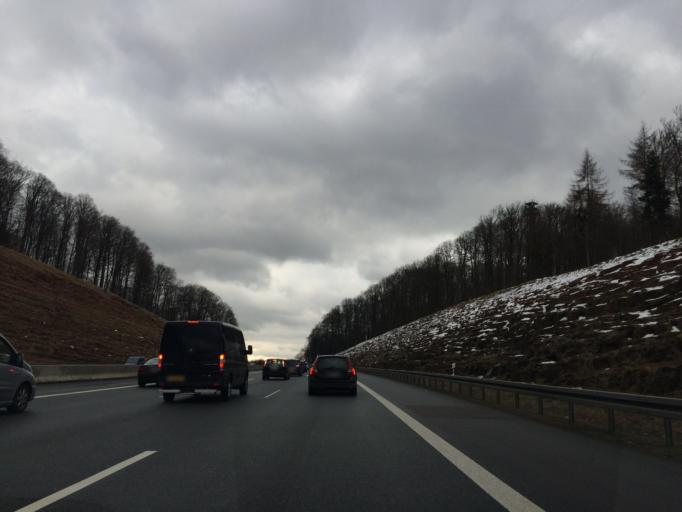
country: DE
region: Bavaria
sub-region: Regierungsbezirk Unterfranken
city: Schollbrunn
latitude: 49.8727
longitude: 9.4478
